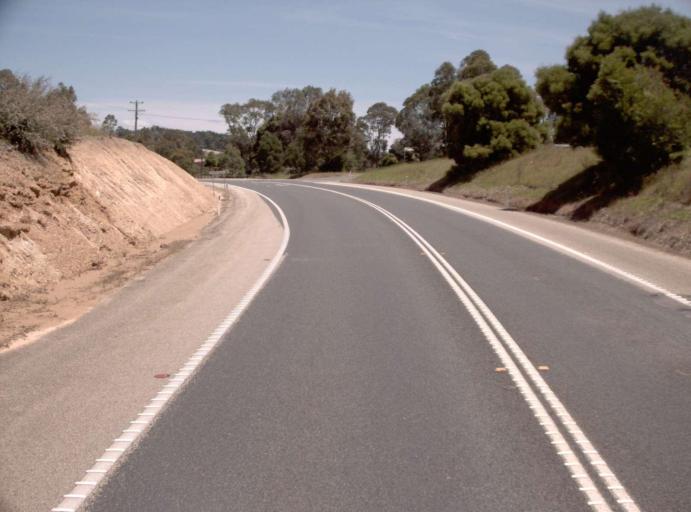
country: AU
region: Victoria
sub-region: East Gippsland
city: Bairnsdale
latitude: -37.7120
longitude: 147.8085
